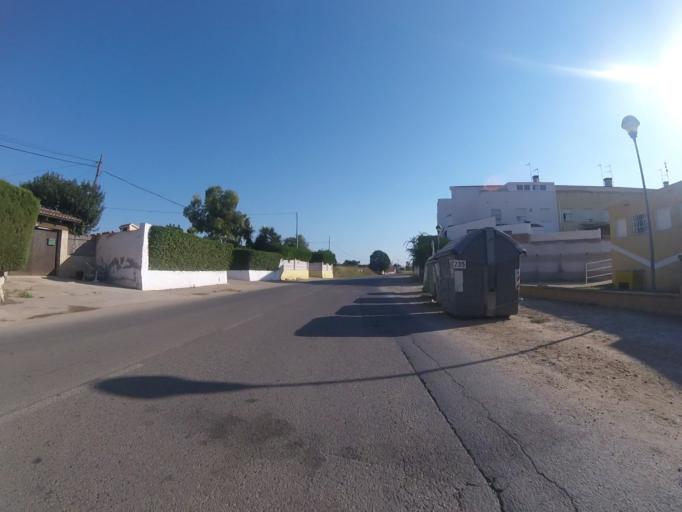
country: ES
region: Valencia
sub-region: Provincia de Castello
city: Benicarlo
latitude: 40.4051
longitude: 0.4159
